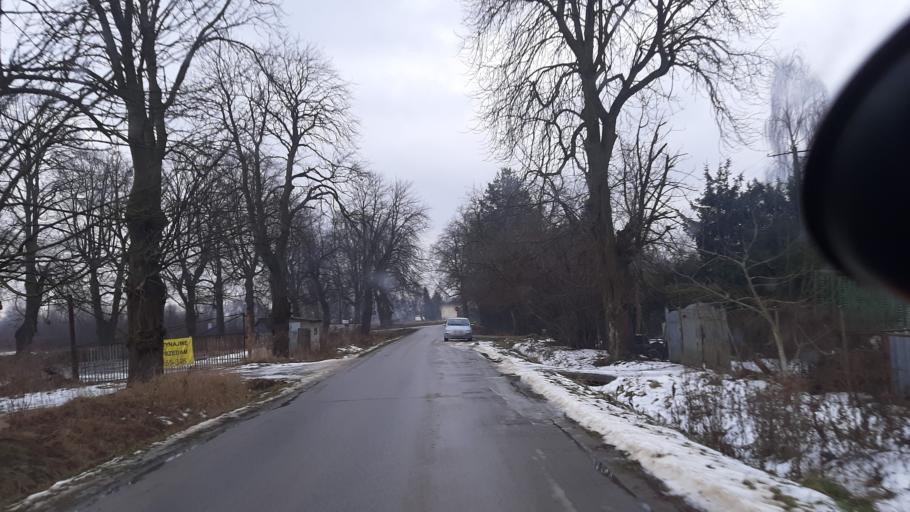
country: PL
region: Lublin Voivodeship
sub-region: Powiat lubelski
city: Lublin
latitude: 51.3338
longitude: 22.5523
